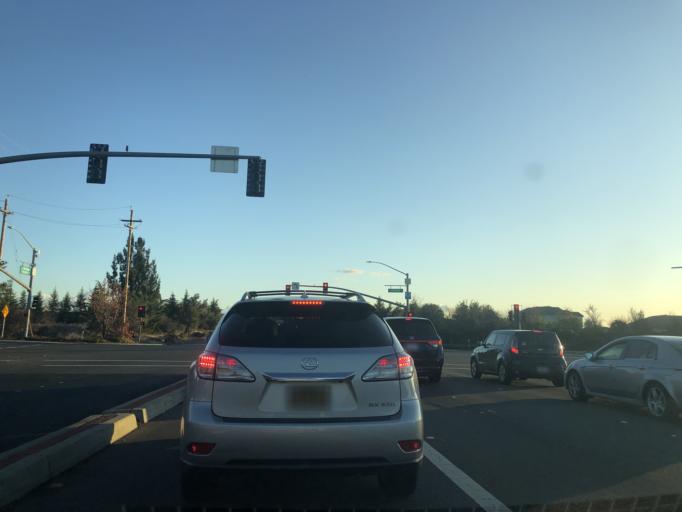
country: US
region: California
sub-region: Sacramento County
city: Antelope
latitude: 38.7522
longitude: -121.3586
